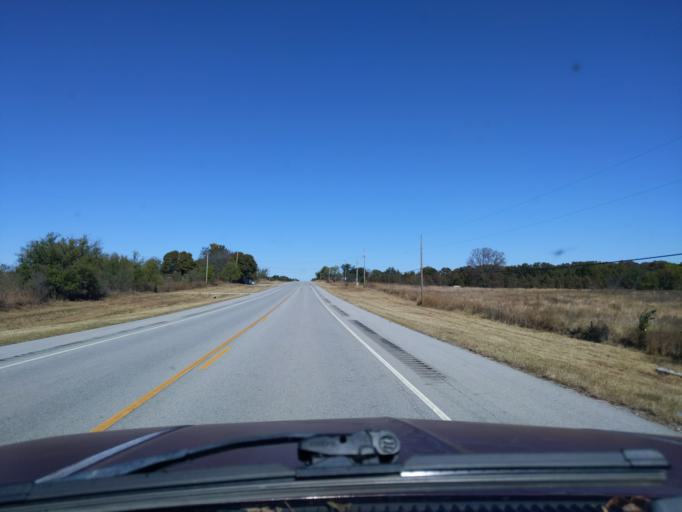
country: US
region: Oklahoma
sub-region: Creek County
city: Bristow
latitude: 35.7539
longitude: -96.3872
